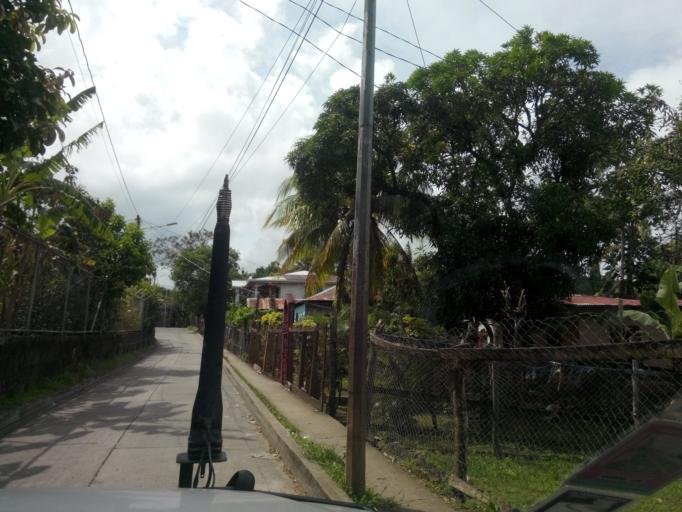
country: NI
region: Atlantico Sur
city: Bluefields
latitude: 12.0102
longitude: -83.7669
